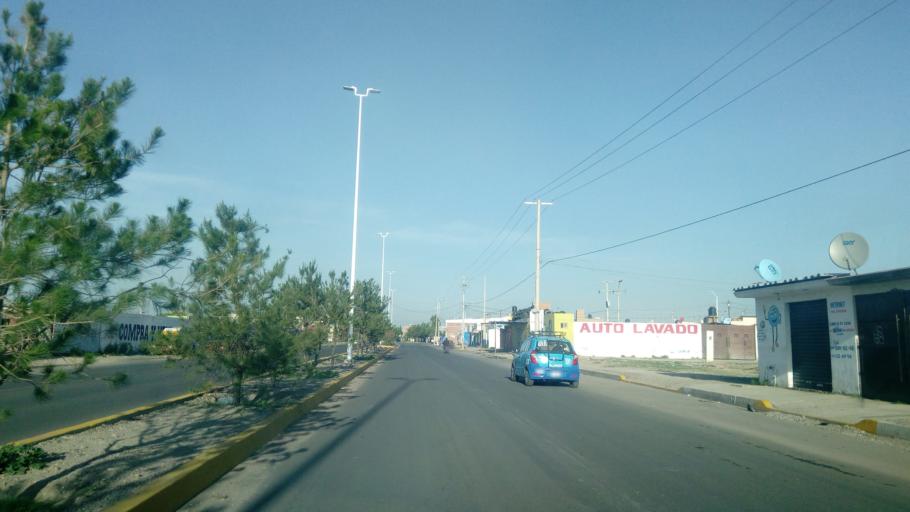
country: MX
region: Durango
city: Victoria de Durango
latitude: 24.0568
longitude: -104.5876
